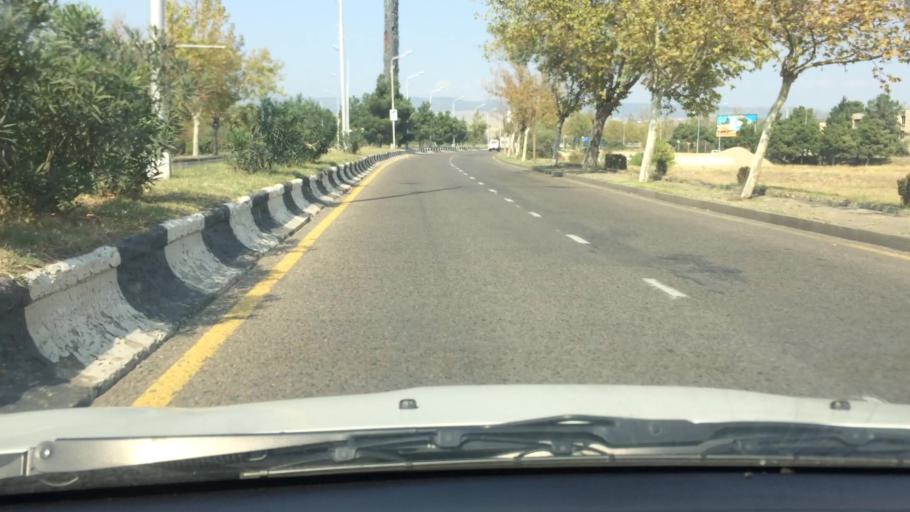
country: GE
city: Didi Lilo
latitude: 41.6892
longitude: 44.9530
